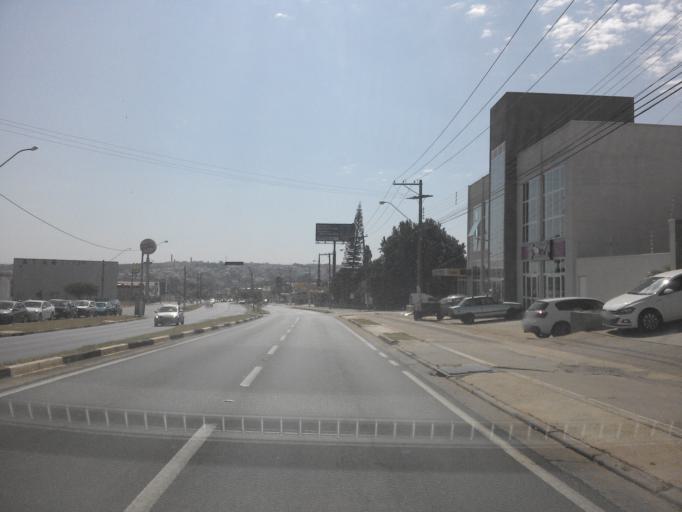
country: BR
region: Sao Paulo
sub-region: Hortolandia
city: Hortolandia
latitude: -22.8714
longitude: -47.2268
